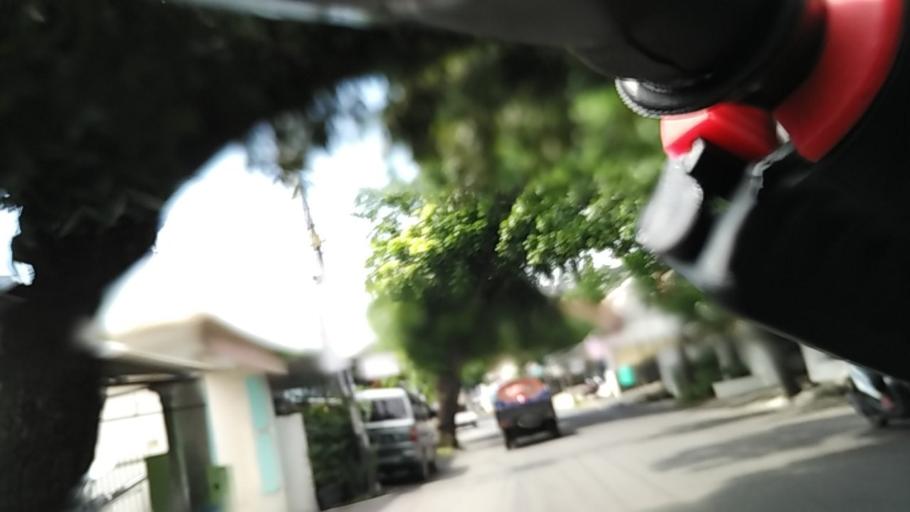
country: ID
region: Central Java
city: Semarang
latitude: -7.0074
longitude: 110.4271
